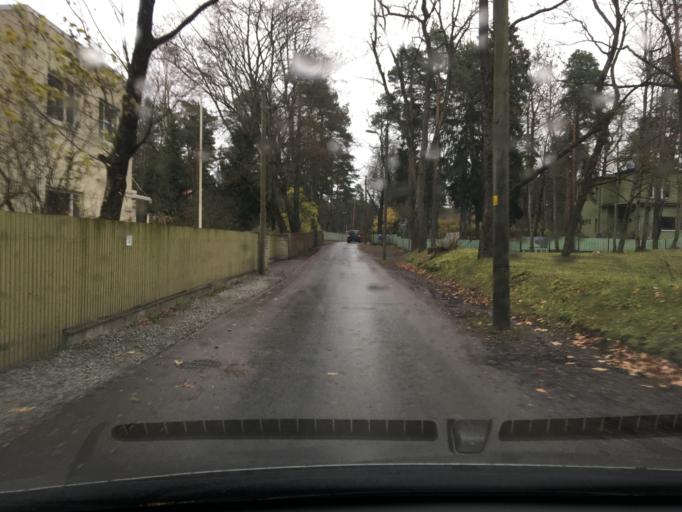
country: EE
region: Harju
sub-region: Tallinna linn
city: Tallinn
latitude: 59.3852
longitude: 24.6922
